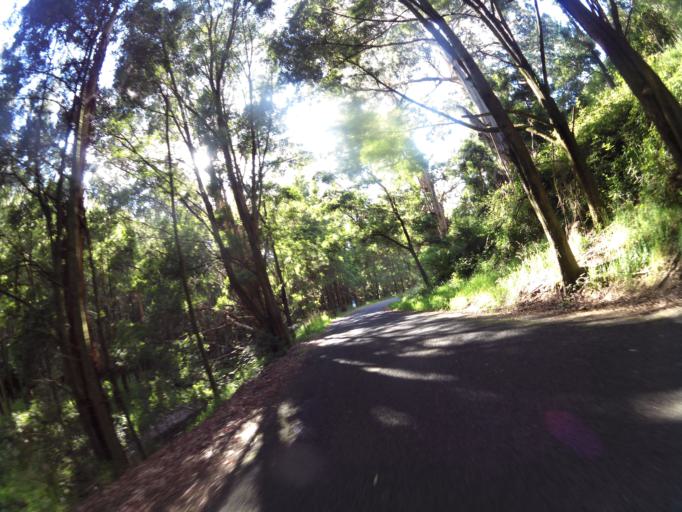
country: AU
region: Victoria
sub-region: Colac-Otway
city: Apollo Bay
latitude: -38.7608
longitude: 143.6292
